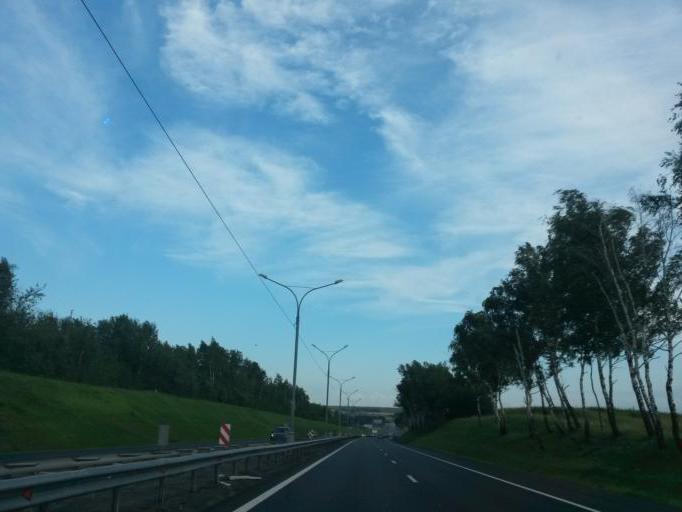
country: RU
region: Moskovskaya
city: Gorki-Leninskiye
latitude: 55.5067
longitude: 37.8350
